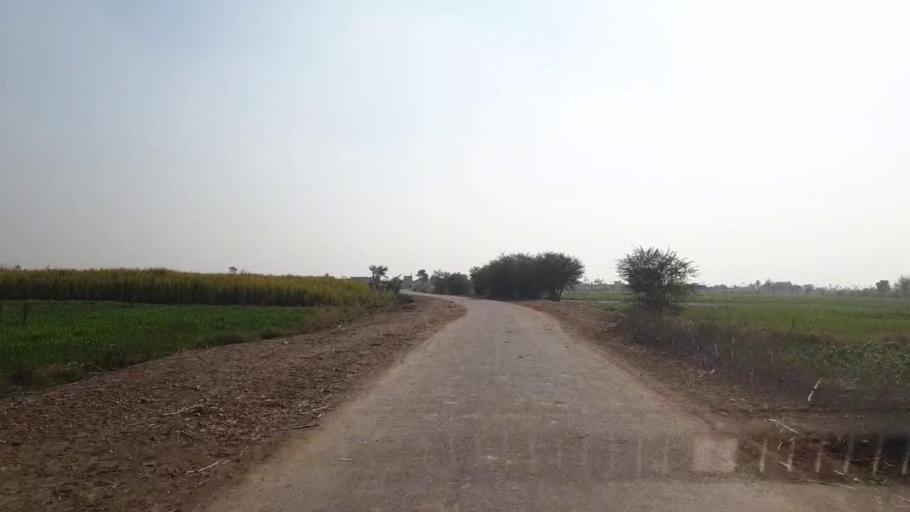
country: PK
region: Sindh
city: Tando Adam
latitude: 25.6637
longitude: 68.5766
